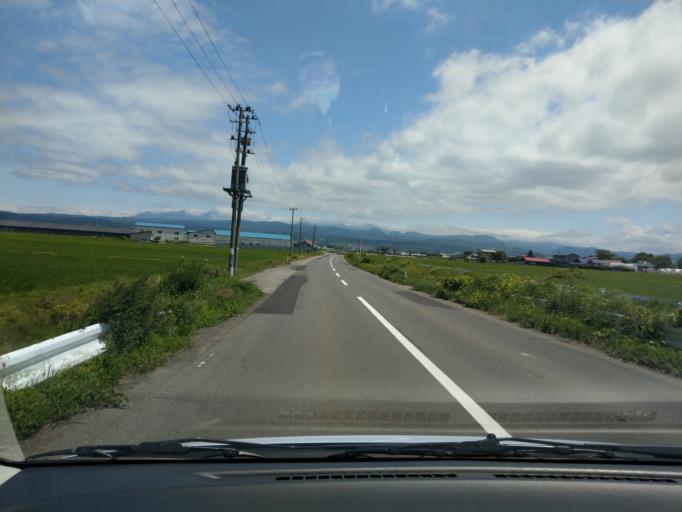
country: JP
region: Aomori
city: Namioka
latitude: 40.6841
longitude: 140.5565
